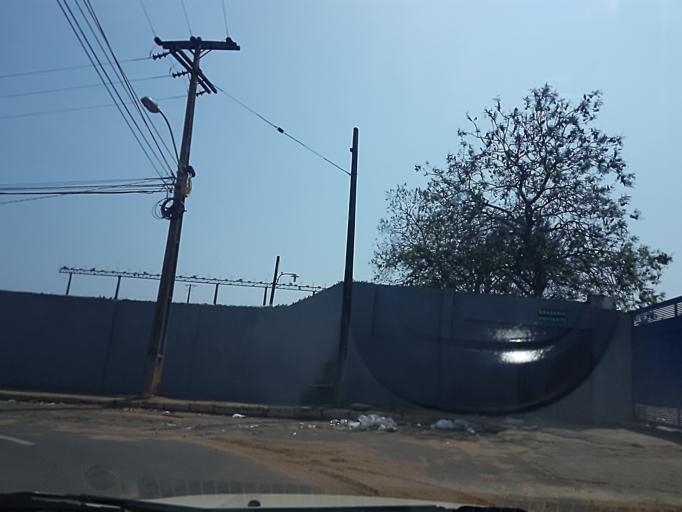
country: PY
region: Asuncion
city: Asuncion
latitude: -25.2988
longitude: -57.6382
